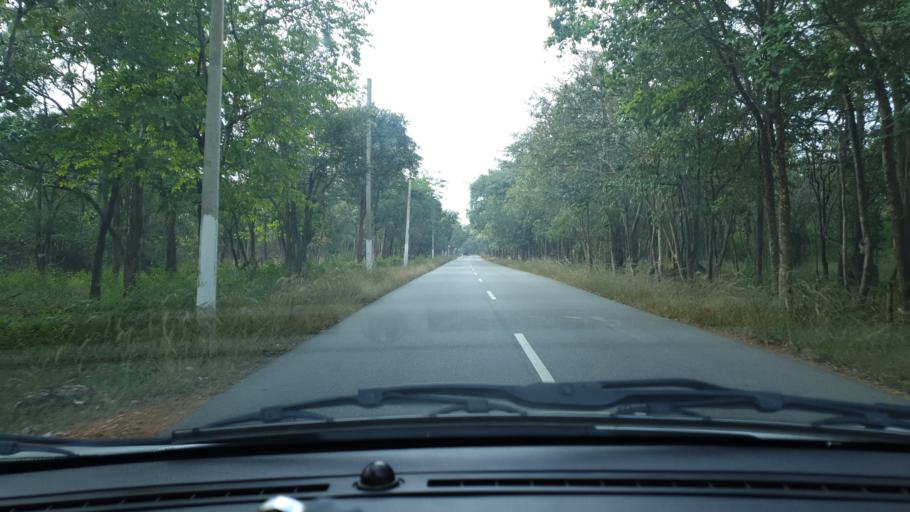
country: IN
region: Andhra Pradesh
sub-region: Kurnool
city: Srisailam
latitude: 16.2857
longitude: 78.7279
